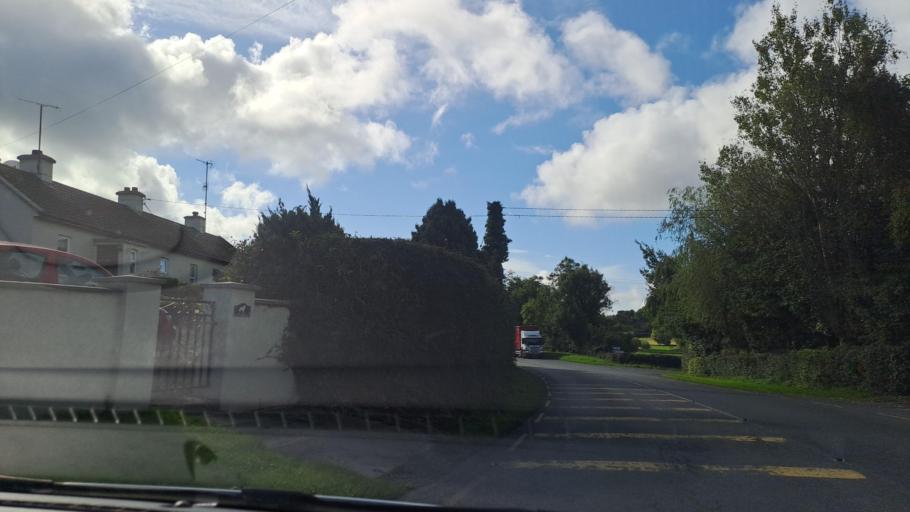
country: IE
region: Ulster
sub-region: An Cabhan
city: Kingscourt
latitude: 53.9383
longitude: -6.7800
